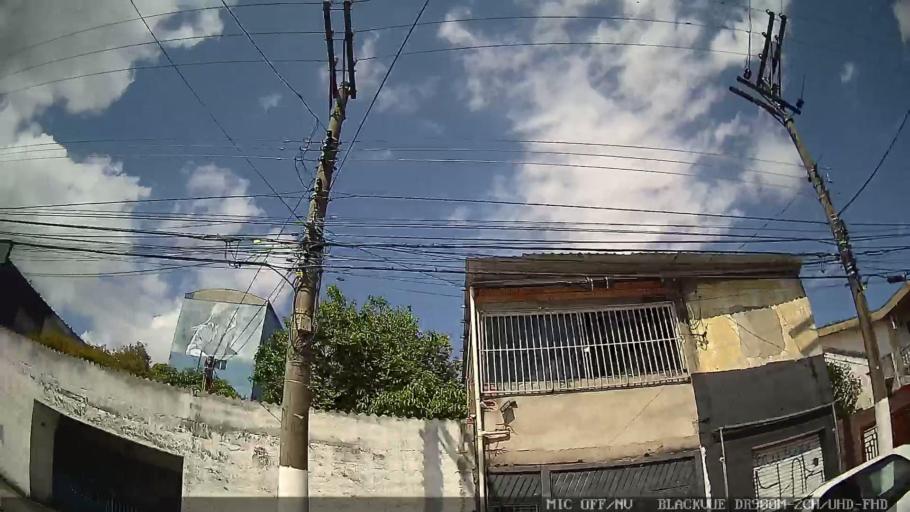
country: BR
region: Sao Paulo
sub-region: Guarulhos
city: Guarulhos
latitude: -23.5035
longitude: -46.4757
